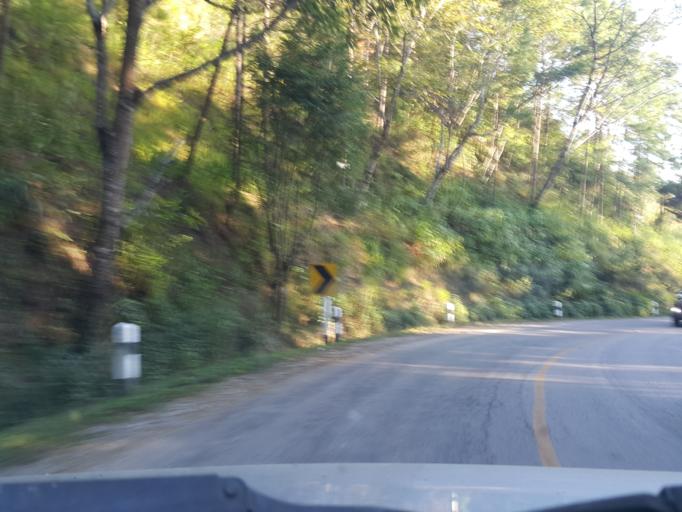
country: TH
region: Mae Hong Son
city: Mae Hi
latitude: 19.2595
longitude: 98.6396
